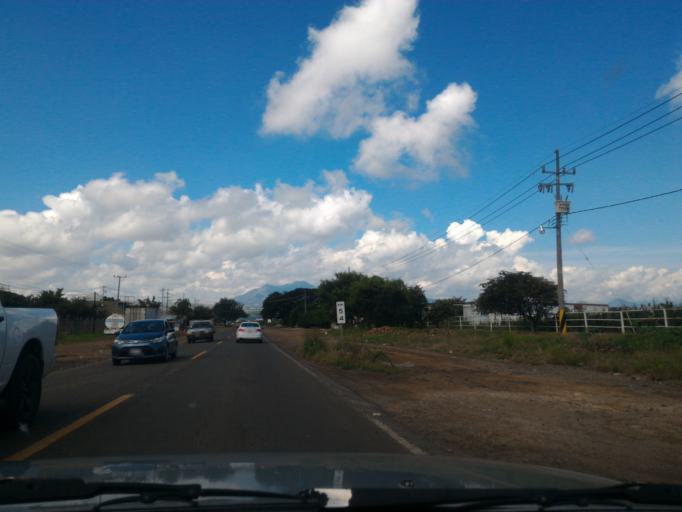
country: MX
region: Jalisco
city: Tequila
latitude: 20.8747
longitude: -103.8058
